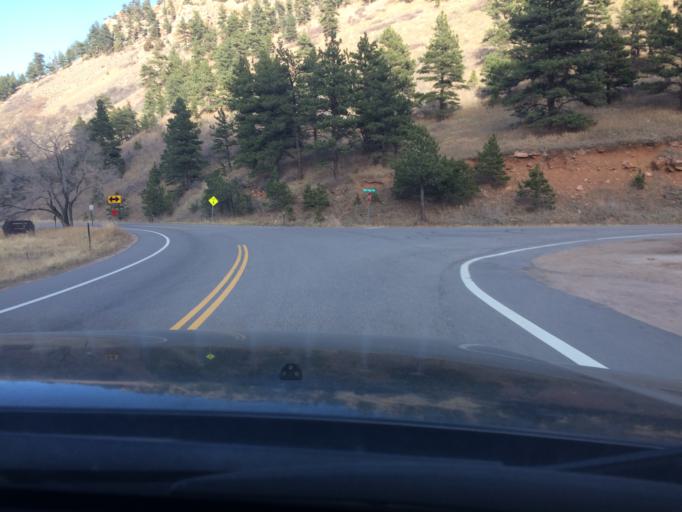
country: US
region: Colorado
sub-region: Boulder County
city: Boulder
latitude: 40.1102
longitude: -105.3065
